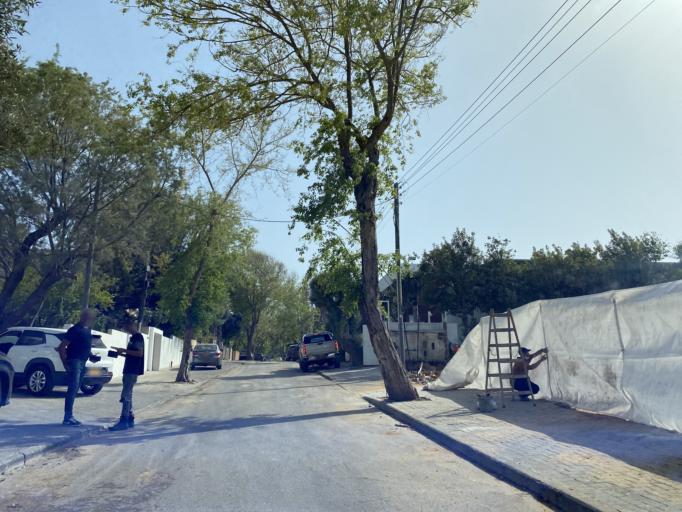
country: IL
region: Tel Aviv
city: Herzliya Pituah
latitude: 32.1771
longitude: 34.8074
